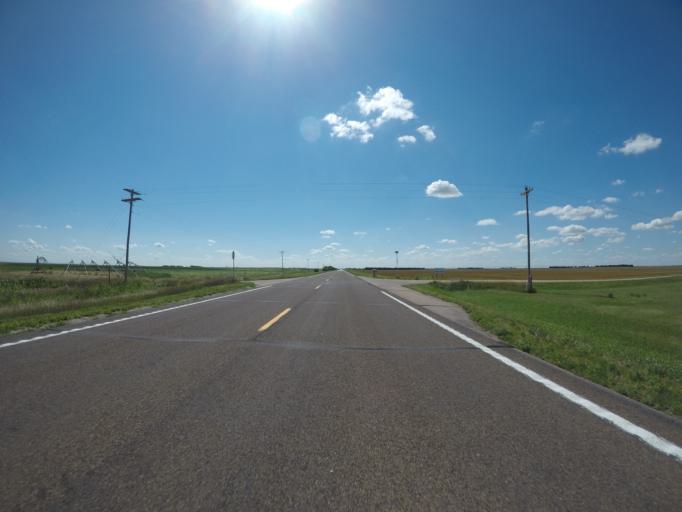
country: US
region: Nebraska
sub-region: Chase County
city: Imperial
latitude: 40.5377
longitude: -101.8750
